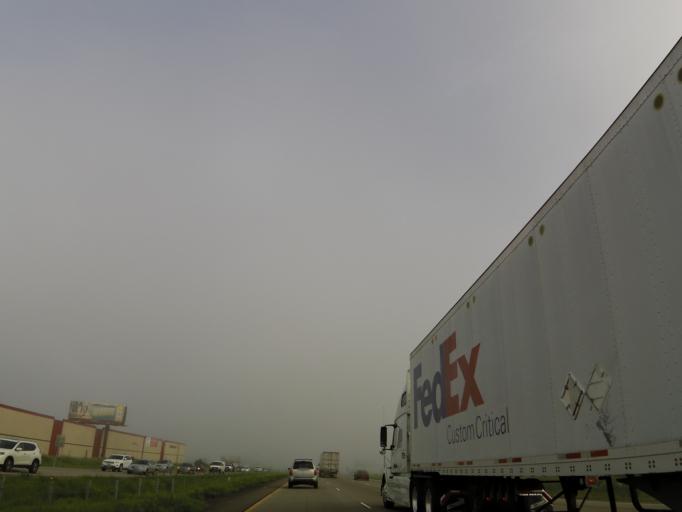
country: US
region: Minnesota
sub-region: Hennepin County
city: Rogers
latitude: 45.1973
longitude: -93.5579
